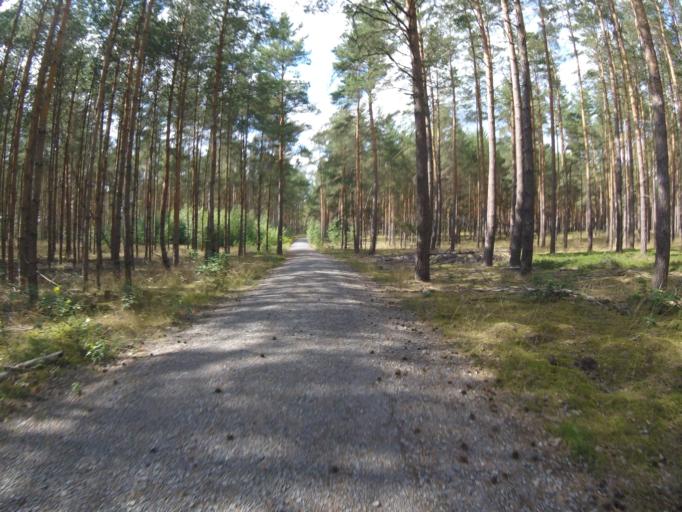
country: DE
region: Brandenburg
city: Halbe
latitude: 52.0628
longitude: 13.7864
